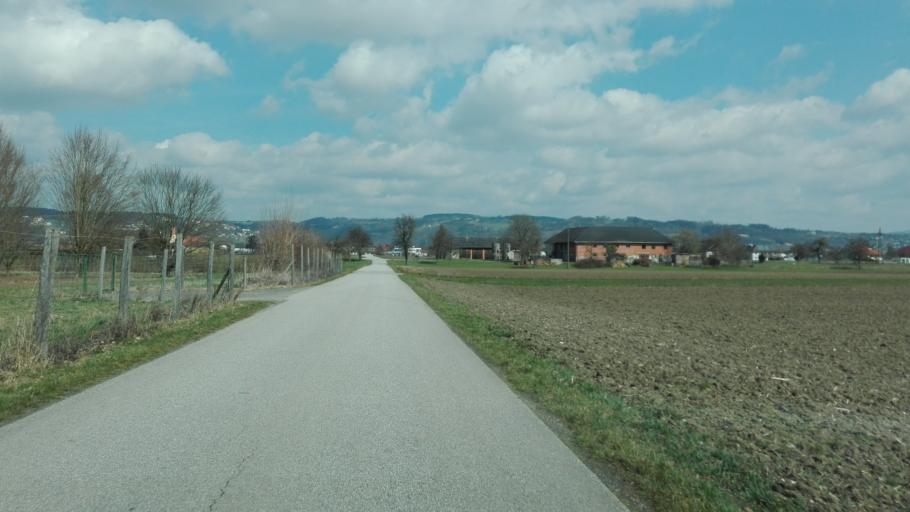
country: AT
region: Upper Austria
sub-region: Politischer Bezirk Urfahr-Umgebung
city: Feldkirchen an der Donau
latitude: 48.3361
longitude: 14.0514
